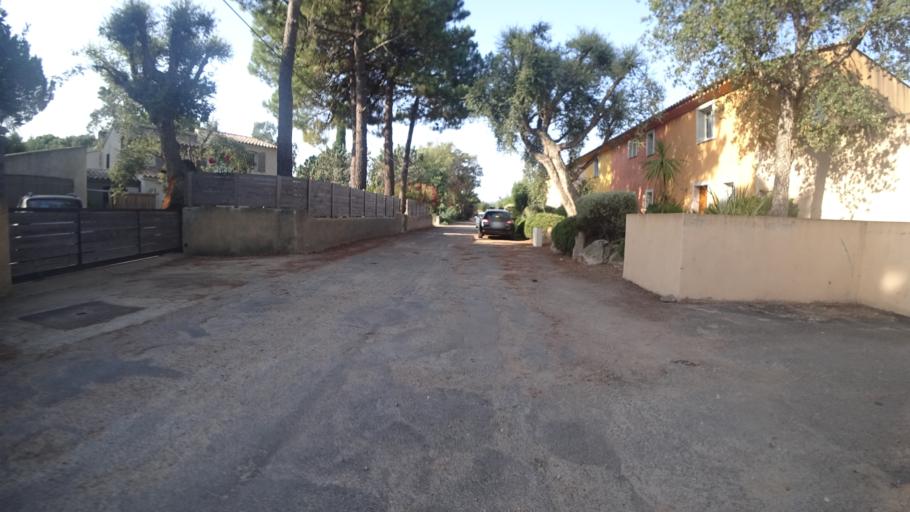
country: FR
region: Corsica
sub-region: Departement de la Corse-du-Sud
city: Porto-Vecchio
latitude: 41.6372
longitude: 9.3416
